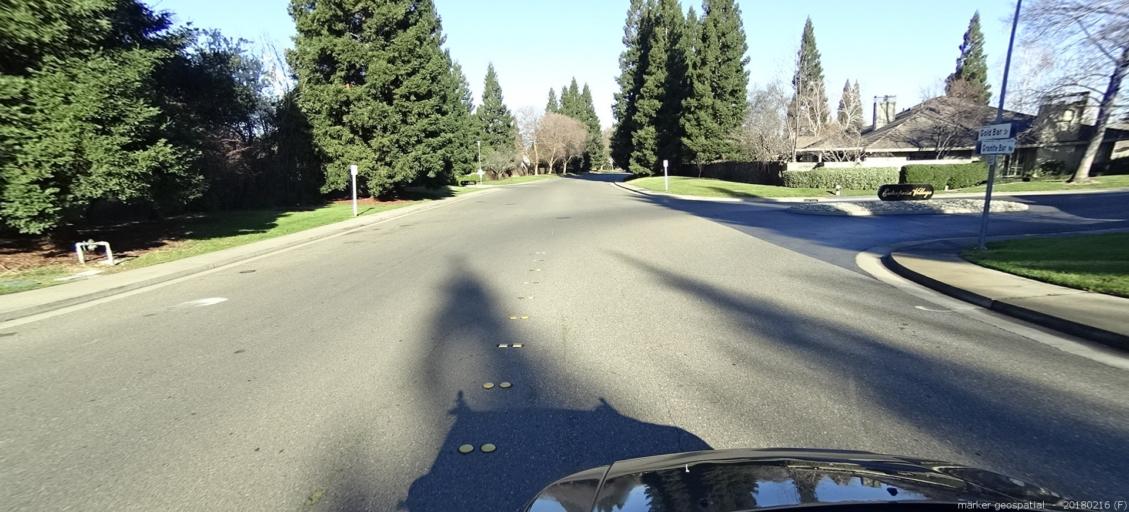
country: US
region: California
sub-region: Sacramento County
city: Gold River
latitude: 38.6244
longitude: -121.2394
